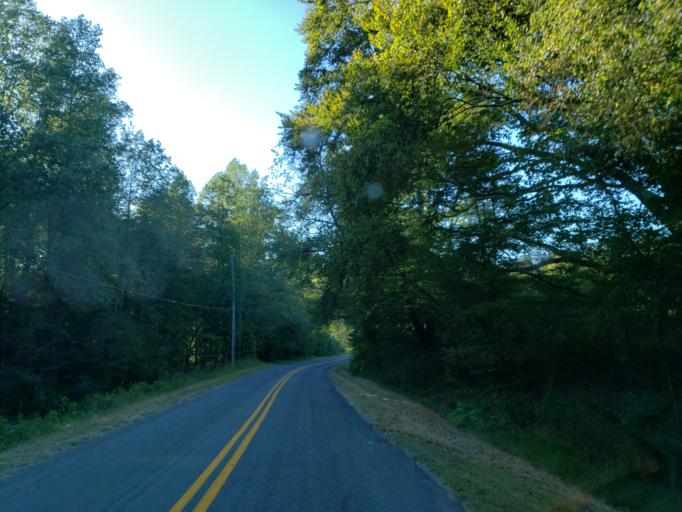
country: US
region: Georgia
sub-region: Pickens County
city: Nelson
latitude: 34.3778
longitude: -84.3954
